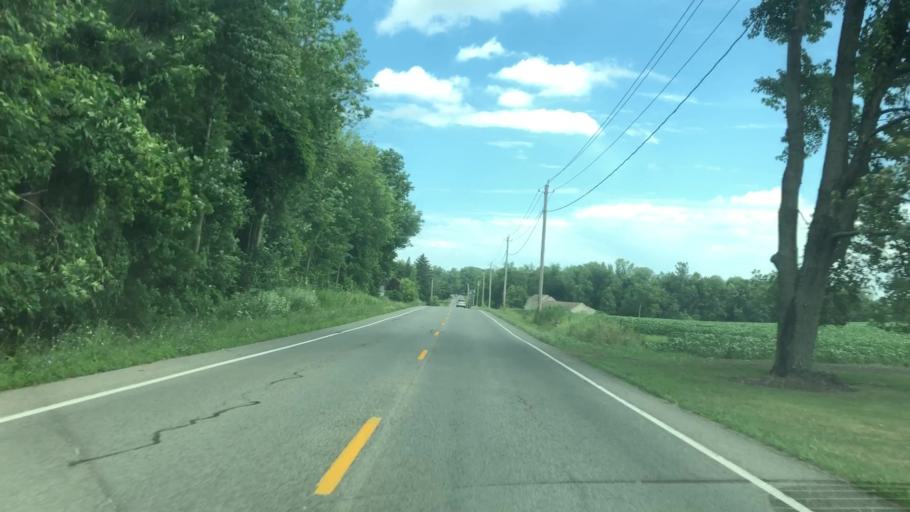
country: US
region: New York
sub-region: Wayne County
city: Macedon
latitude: 43.1171
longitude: -77.3525
